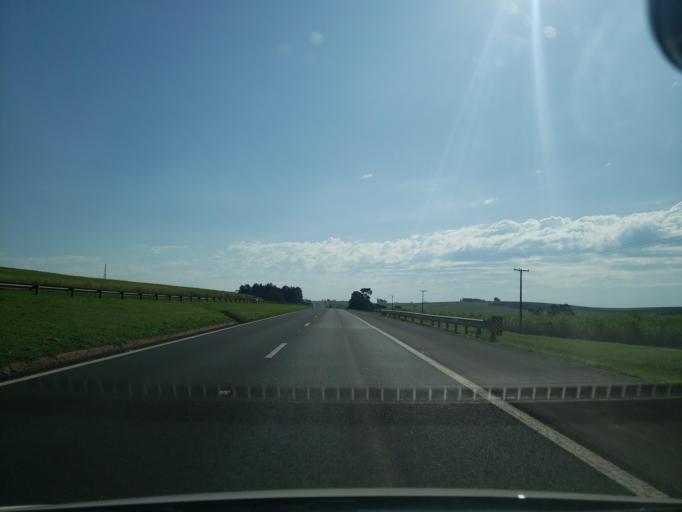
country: BR
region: Sao Paulo
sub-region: Penapolis
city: Penapolis
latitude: -21.5234
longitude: -49.9956
